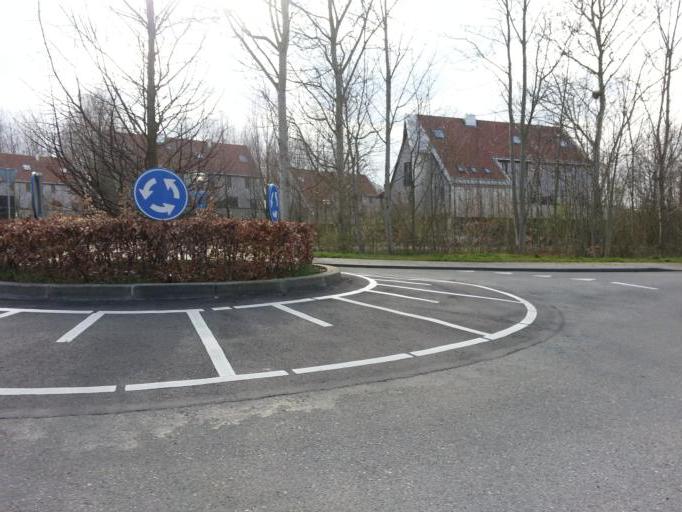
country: NL
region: Flevoland
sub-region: Gemeente Almere
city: Almere Stad
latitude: 52.3989
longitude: 5.3161
